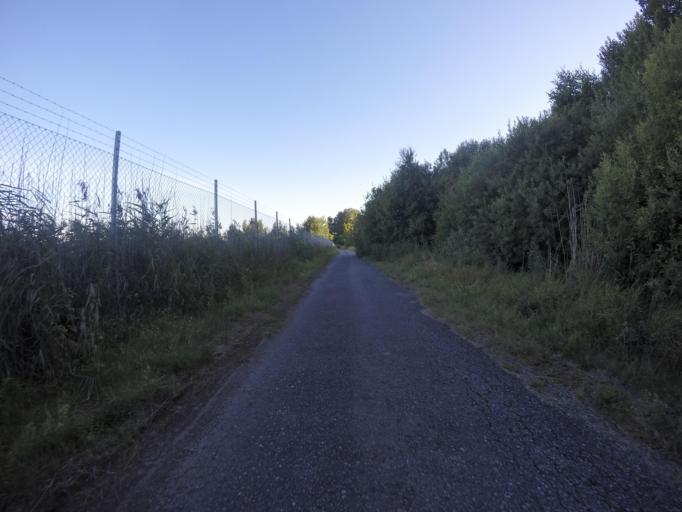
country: SE
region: Vaestmanland
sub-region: Vasteras
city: Vasteras
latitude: 59.5786
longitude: 16.6251
